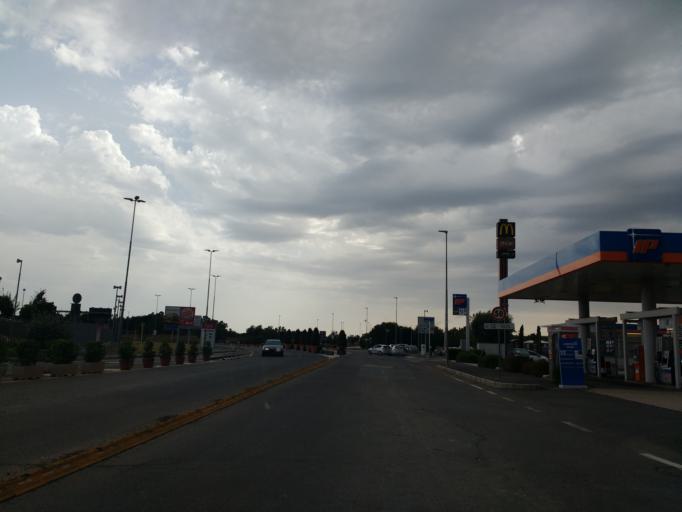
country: IT
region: Latium
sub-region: Citta metropolitana di Roma Capitale
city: Monte Migliore-La Selvotta
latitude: 41.7155
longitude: 12.4445
